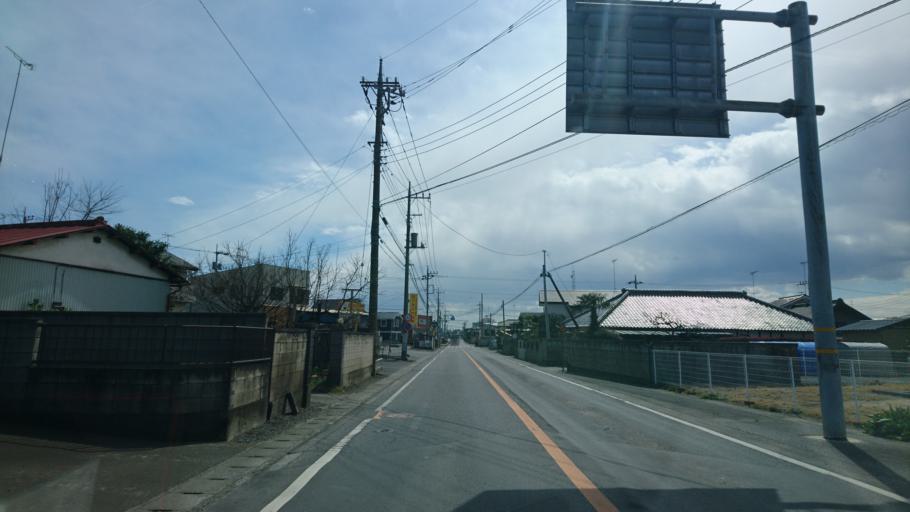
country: JP
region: Ibaraki
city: Yuki
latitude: 36.2909
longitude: 139.9140
